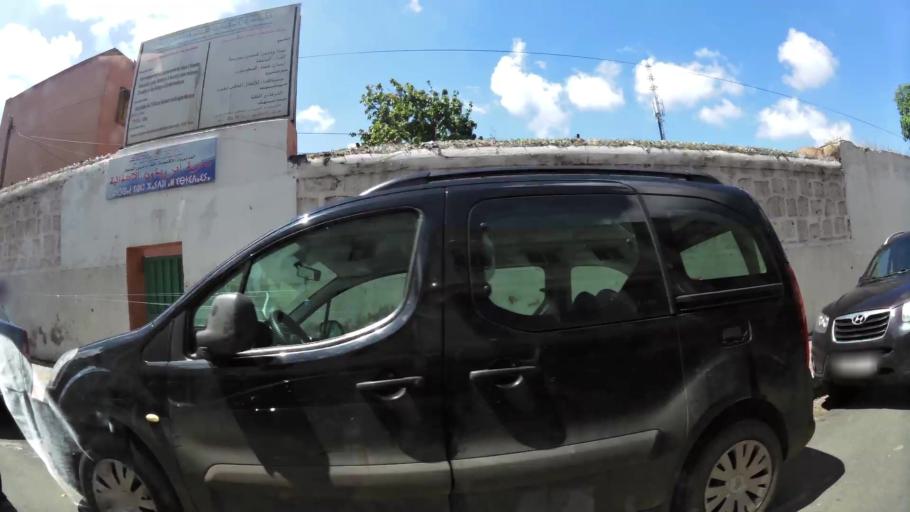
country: MA
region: Grand Casablanca
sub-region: Casablanca
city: Casablanca
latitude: 33.5672
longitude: -7.6039
